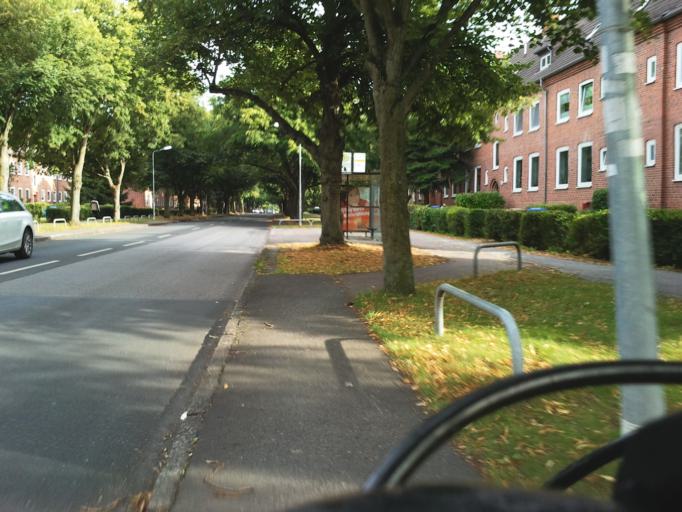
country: DE
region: Mecklenburg-Vorpommern
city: Kritzmow
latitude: 54.0938
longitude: 12.0851
